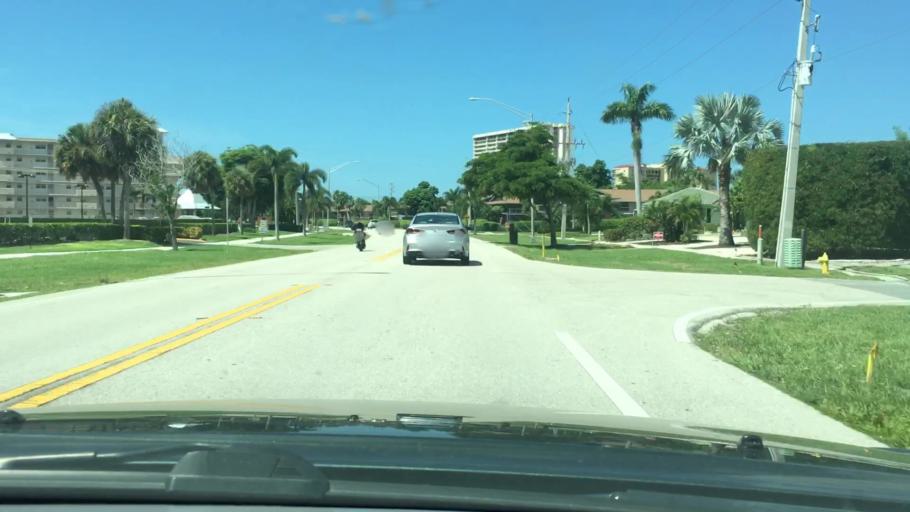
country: US
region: Florida
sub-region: Collier County
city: Marco
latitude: 25.9371
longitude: -81.7278
